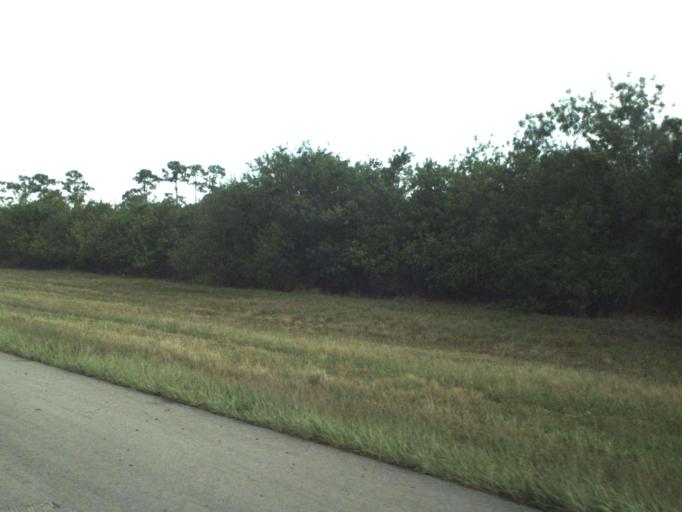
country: US
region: Florida
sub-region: Saint Lucie County
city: Lakewood Park
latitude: 27.4747
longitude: -80.4301
